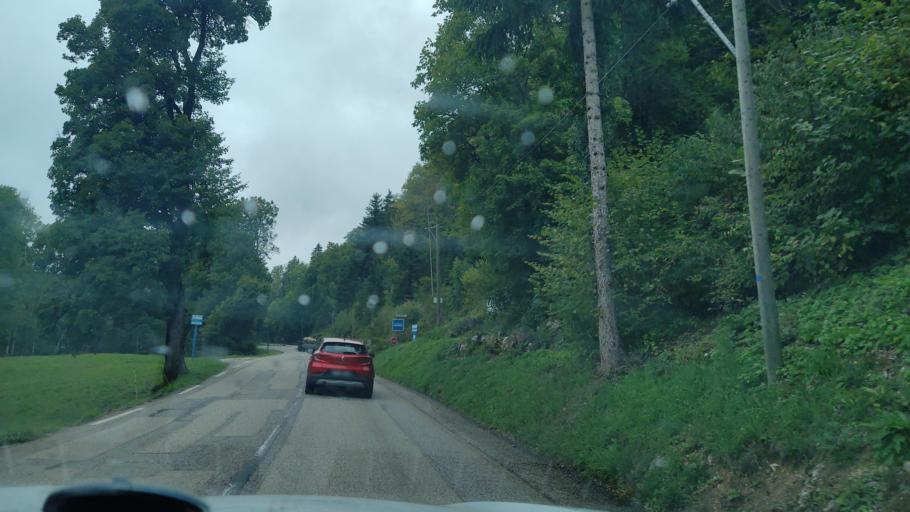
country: FR
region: Rhone-Alpes
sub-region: Departement de l'Isere
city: Barraux
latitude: 45.4421
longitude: 5.8799
